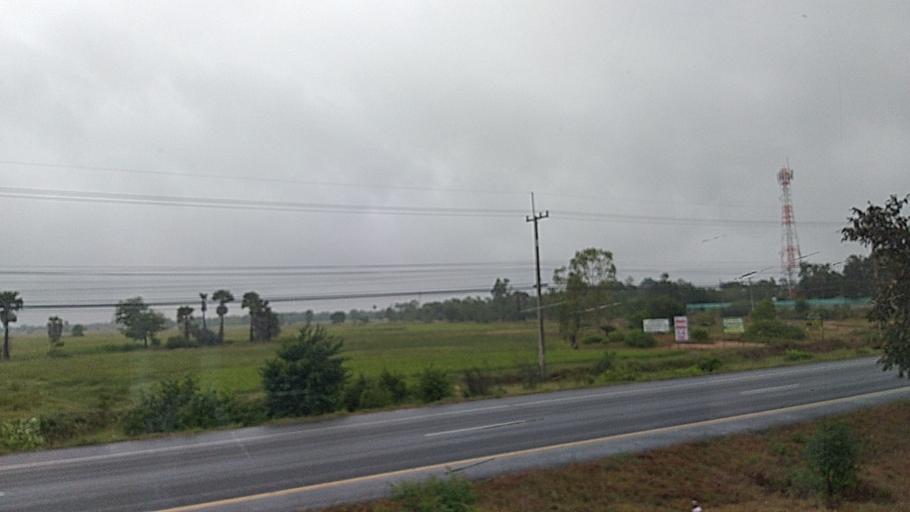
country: TH
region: Nakhon Ratchasima
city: Non Sung
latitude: 15.1418
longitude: 102.3171
